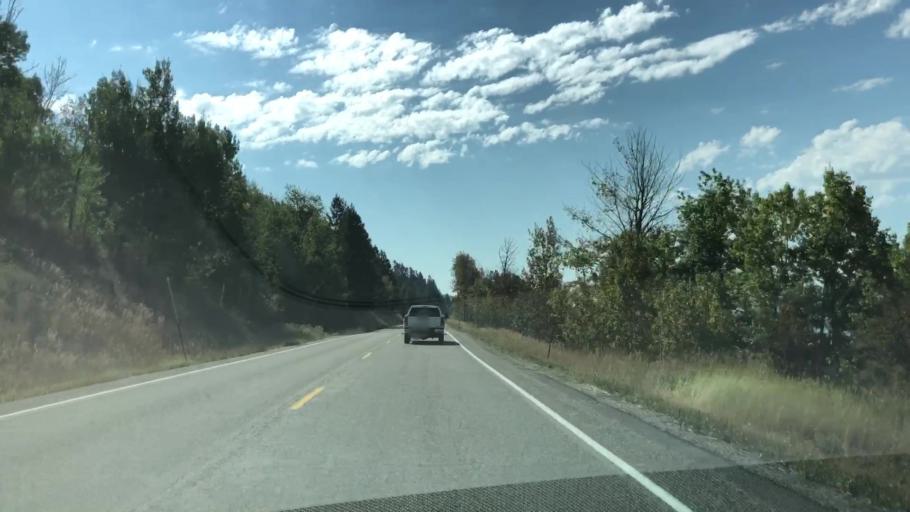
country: US
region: Idaho
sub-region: Teton County
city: Victor
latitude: 43.2923
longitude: -111.1245
